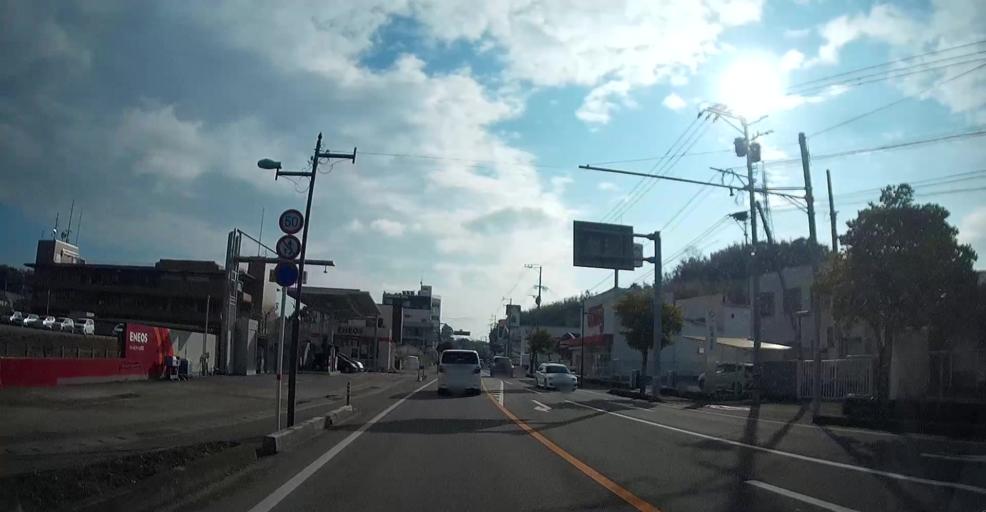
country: JP
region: Kumamoto
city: Yatsushiro
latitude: 32.5885
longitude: 130.4297
